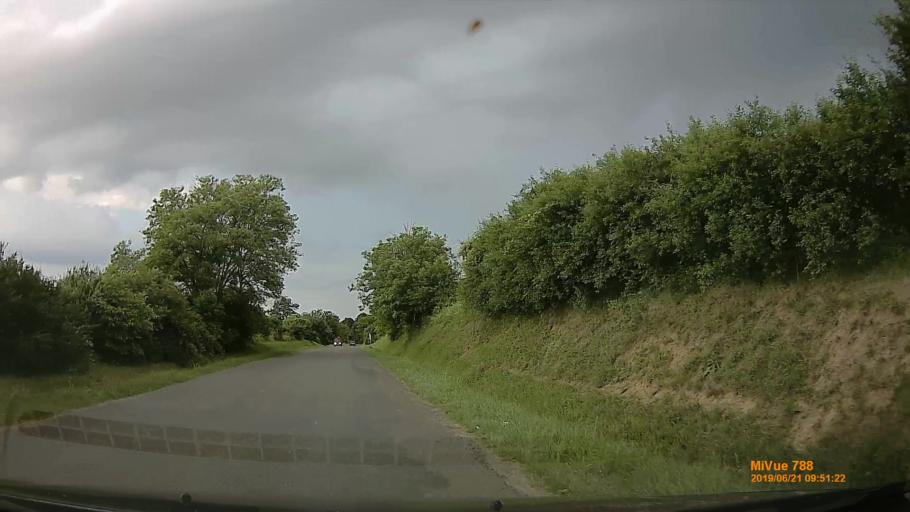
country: HU
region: Baranya
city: Sasd
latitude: 46.2527
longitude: 18.0226
